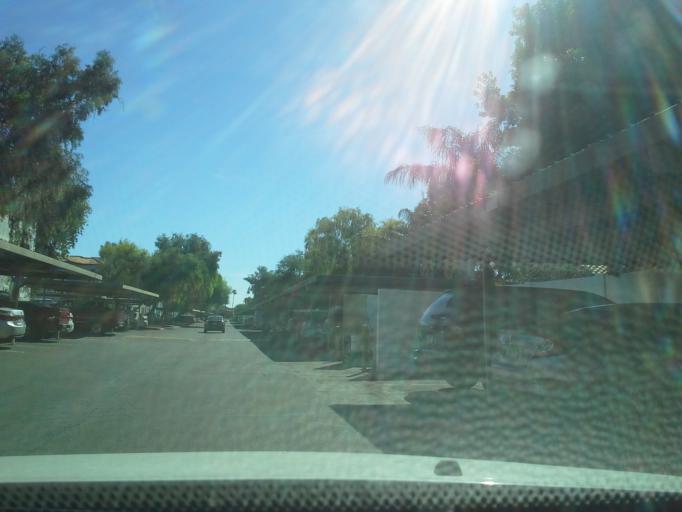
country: US
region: Arizona
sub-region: Maricopa County
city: Paradise Valley
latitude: 33.6436
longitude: -111.9795
